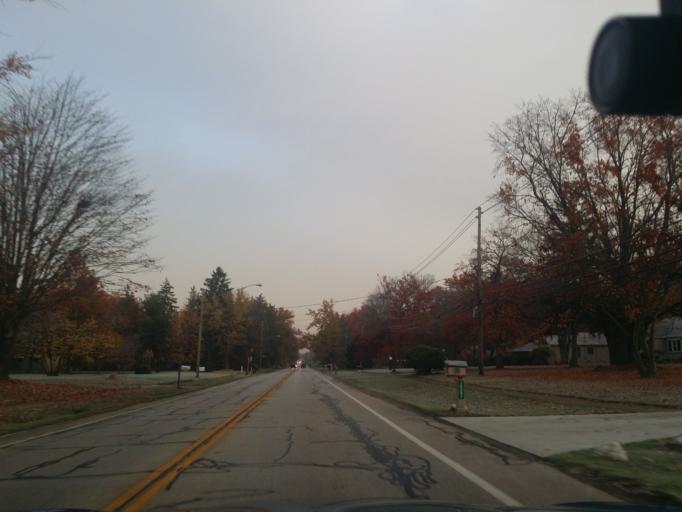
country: US
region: Ohio
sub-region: Cuyahoga County
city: Strongsville
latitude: 41.3347
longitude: -81.8576
